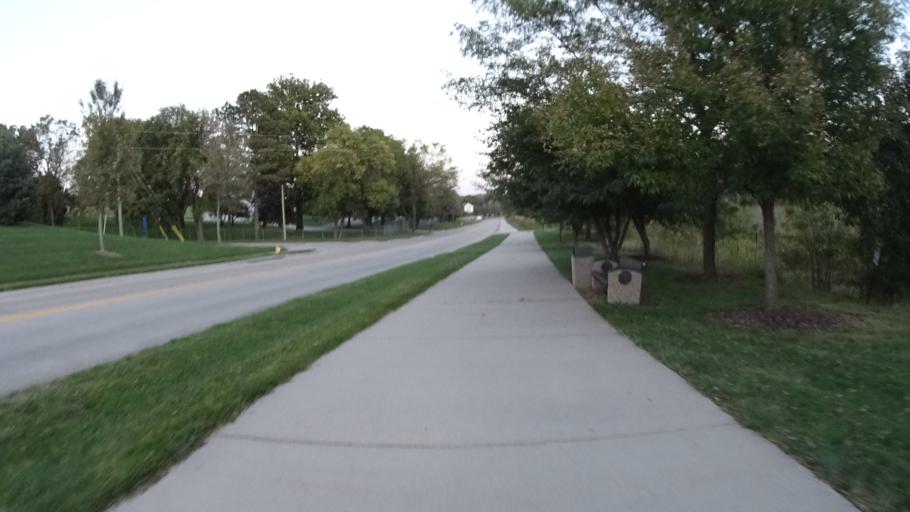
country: US
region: Nebraska
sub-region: Sarpy County
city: Papillion
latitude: 41.1382
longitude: -95.9818
